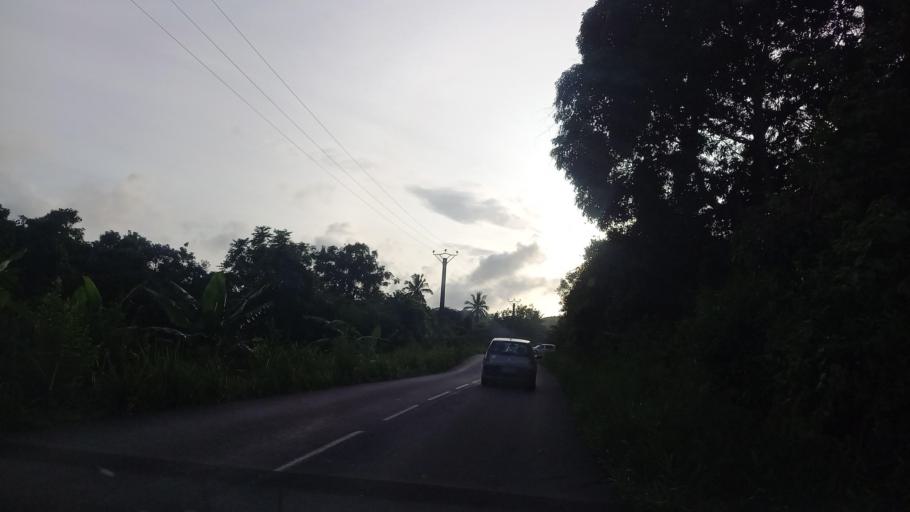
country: YT
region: M'Tsangamouji
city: M'Tsangamouji
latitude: -12.7632
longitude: 45.1003
